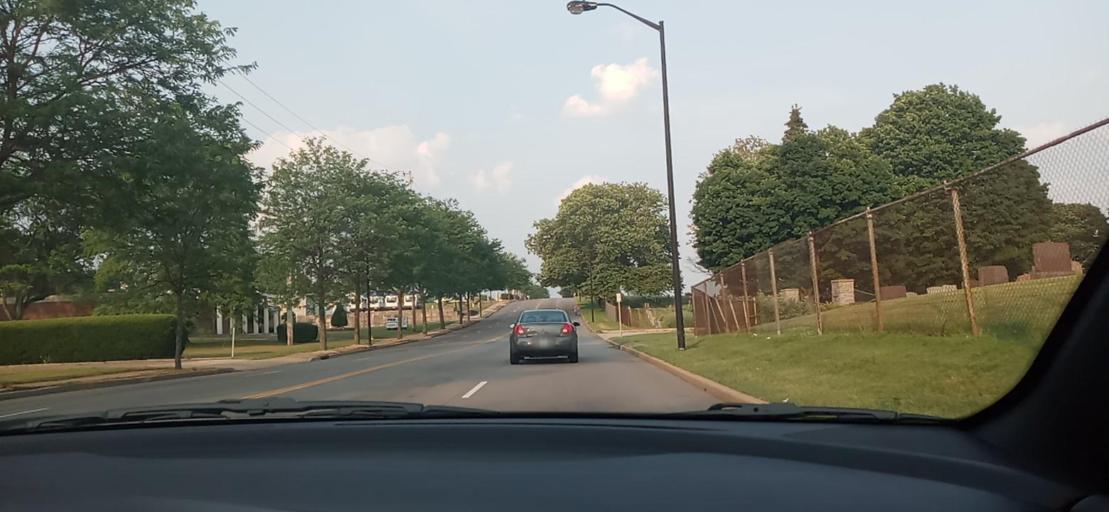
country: US
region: Ohio
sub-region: Summit County
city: Portage Lakes
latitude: 41.0287
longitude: -81.5239
